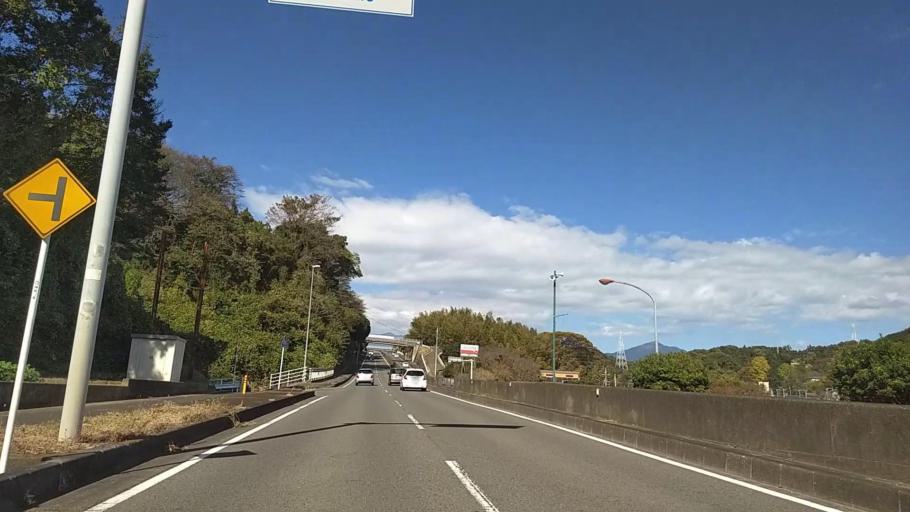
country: JP
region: Kanagawa
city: Ninomiya
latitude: 35.3179
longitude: 139.2411
